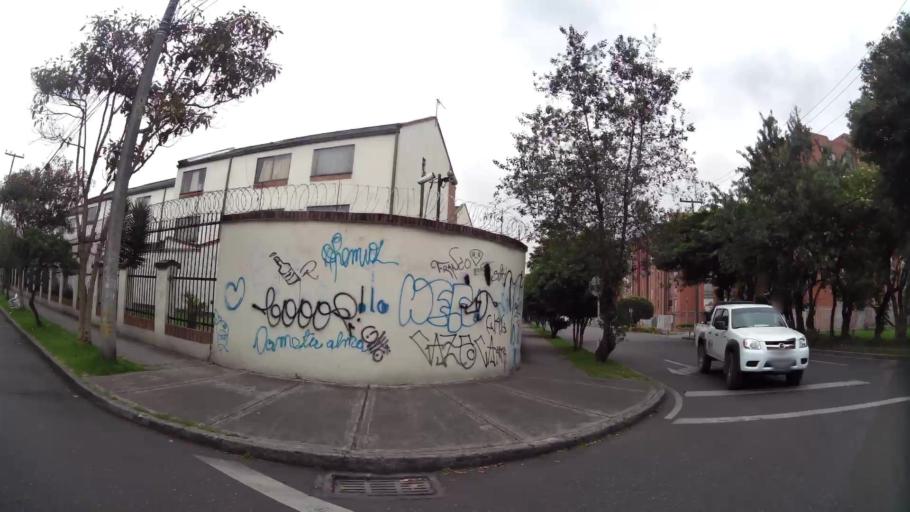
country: CO
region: Bogota D.C.
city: Bogota
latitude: 4.6726
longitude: -74.1237
